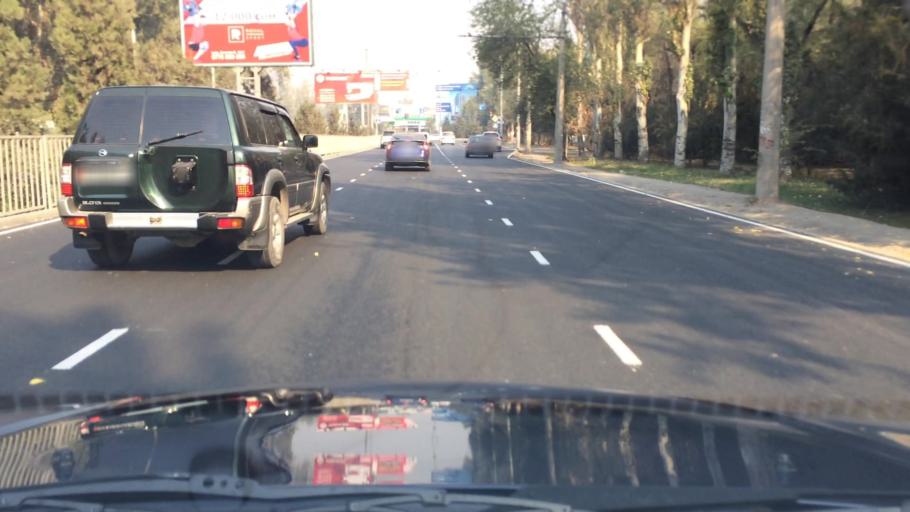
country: KG
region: Chuy
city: Lebedinovka
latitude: 42.8736
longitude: 74.6372
